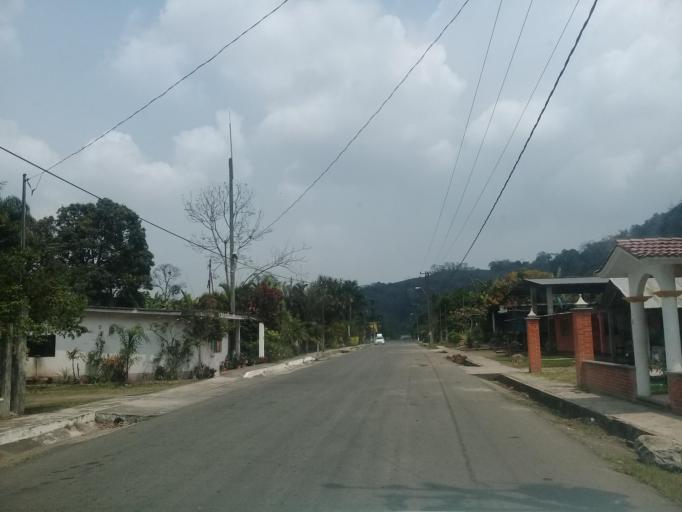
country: MX
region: Veracruz
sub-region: Cordoba
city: San Jose de Tapia
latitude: 18.8225
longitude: -96.9801
